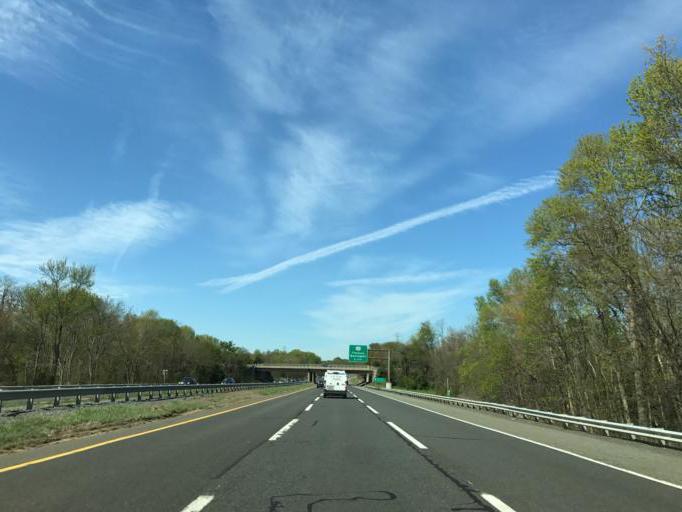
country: US
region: New Jersey
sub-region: Burlington County
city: Roebling
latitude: 40.0955
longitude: -74.7482
